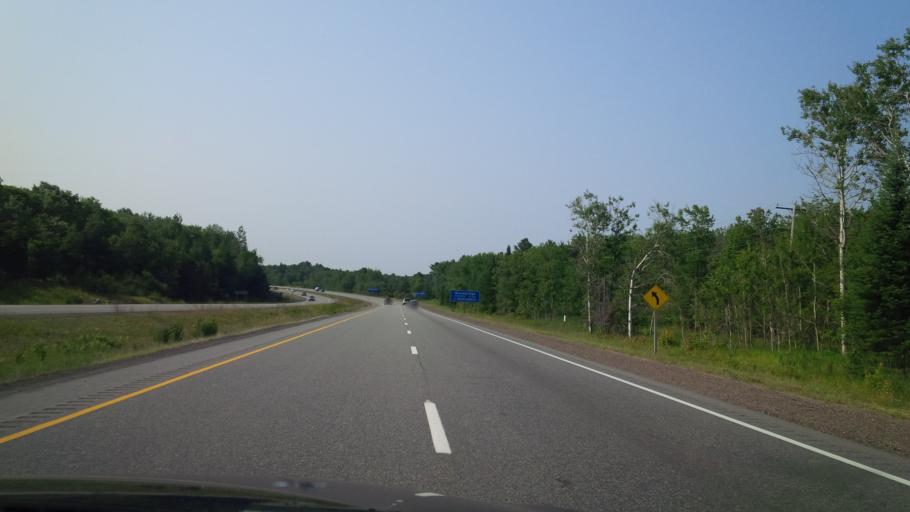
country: CA
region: Ontario
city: Bracebridge
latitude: 45.0672
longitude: -79.2973
